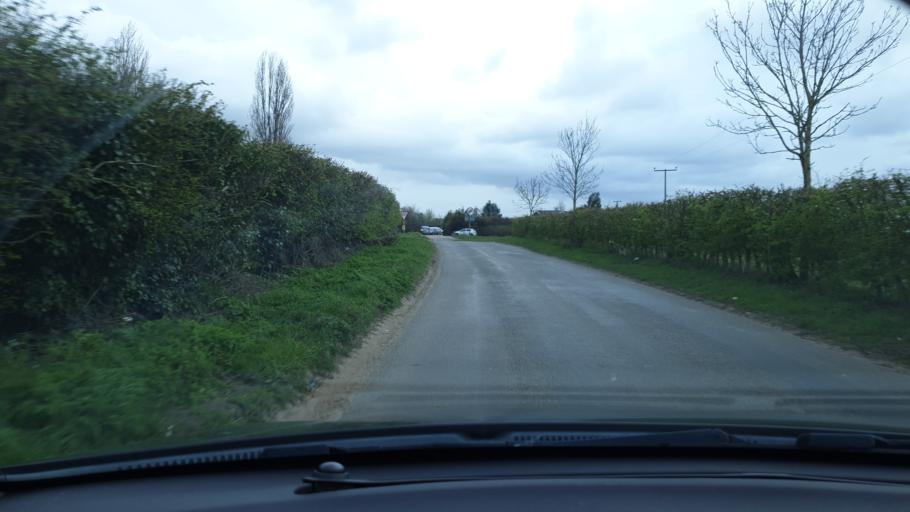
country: GB
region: England
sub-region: Essex
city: Mistley
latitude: 51.9242
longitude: 1.1768
